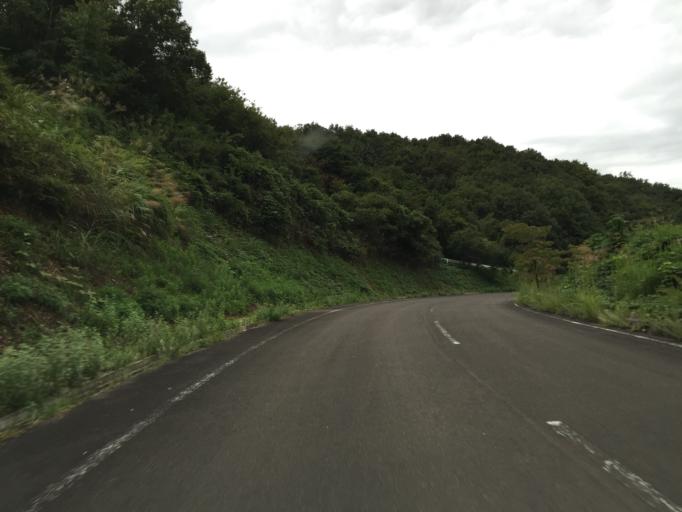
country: JP
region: Fukushima
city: Hobaramachi
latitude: 37.7827
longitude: 140.5143
